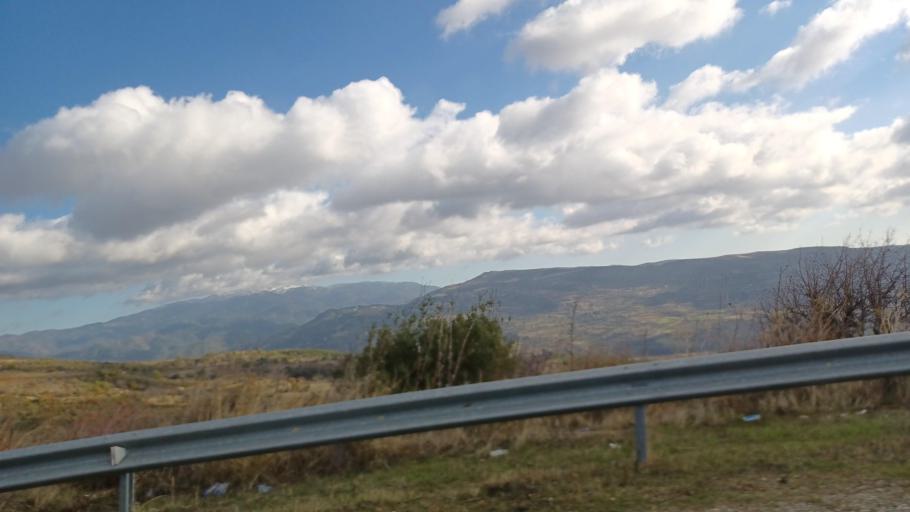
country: CY
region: Limassol
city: Pachna
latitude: 34.8502
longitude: 32.6953
